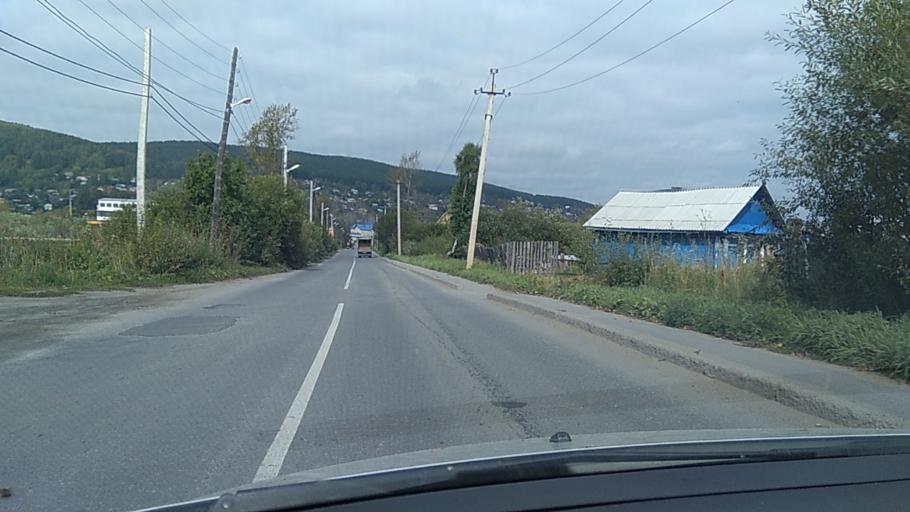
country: RU
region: Chelyabinsk
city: Zlatoust
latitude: 55.1714
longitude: 59.7075
